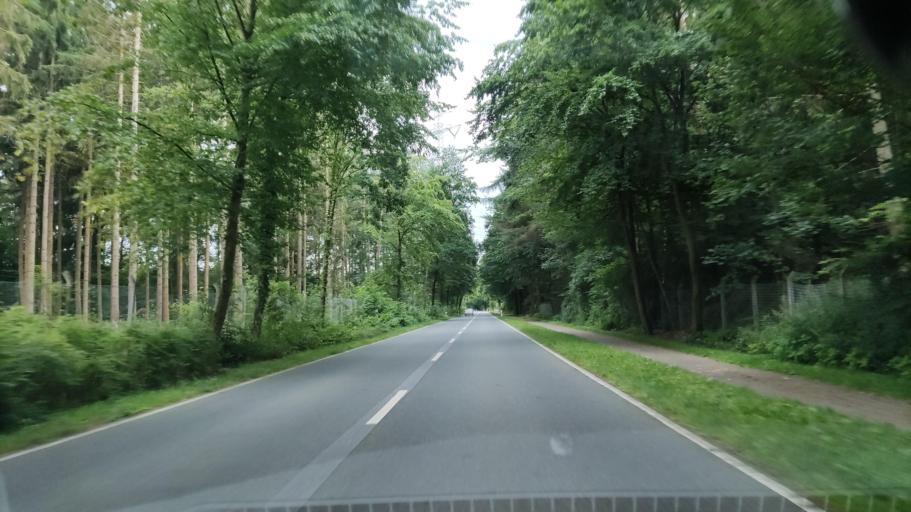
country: DE
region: Lower Saxony
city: Tespe
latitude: 53.4196
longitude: 10.4244
